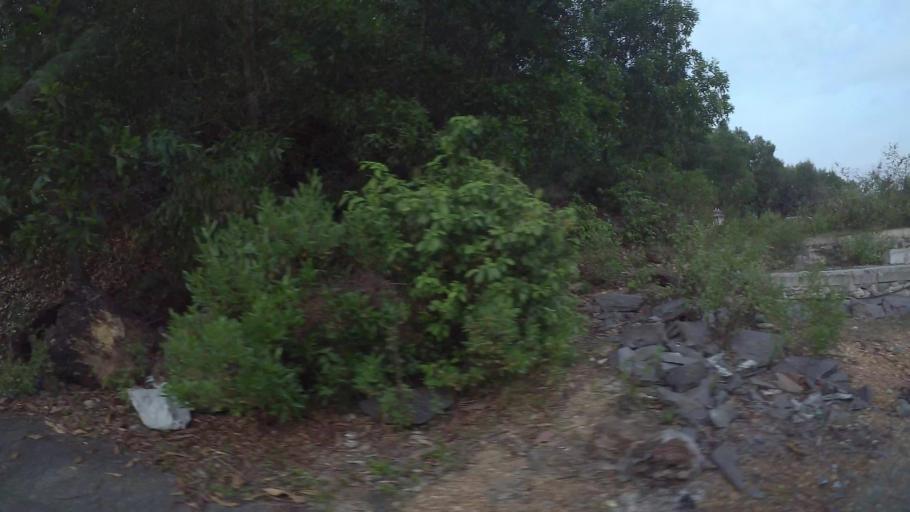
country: VN
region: Da Nang
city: Lien Chieu
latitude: 16.0622
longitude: 108.1205
